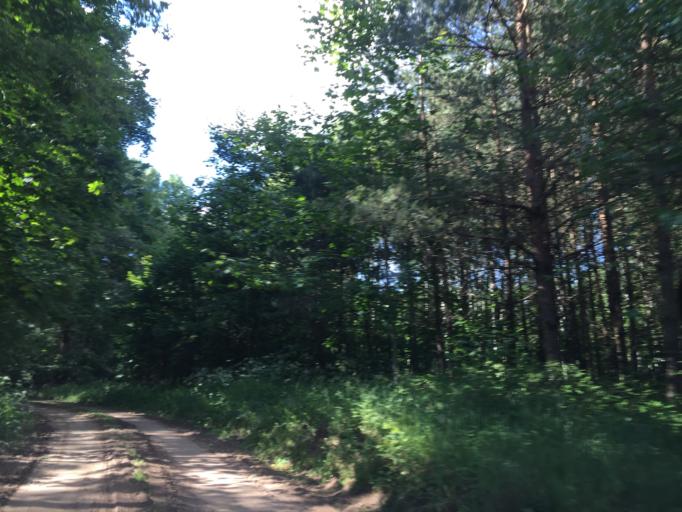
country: LV
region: Vecumnieki
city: Vecumnieki
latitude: 56.4361
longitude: 24.5948
